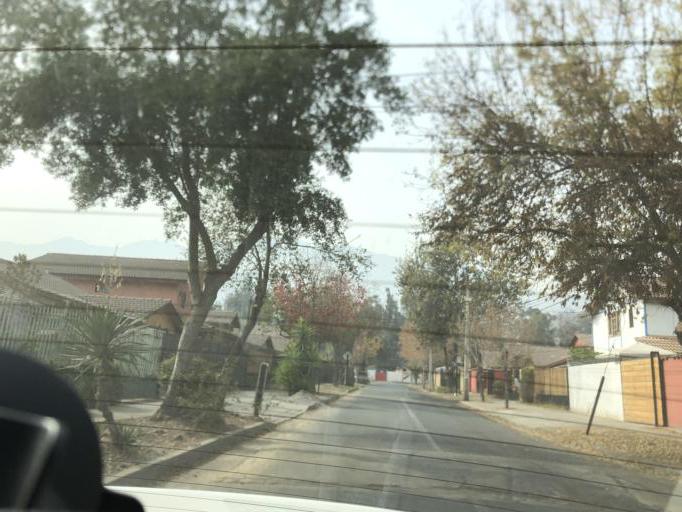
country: CL
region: Santiago Metropolitan
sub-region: Provincia de Cordillera
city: Puente Alto
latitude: -33.5497
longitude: -70.5560
